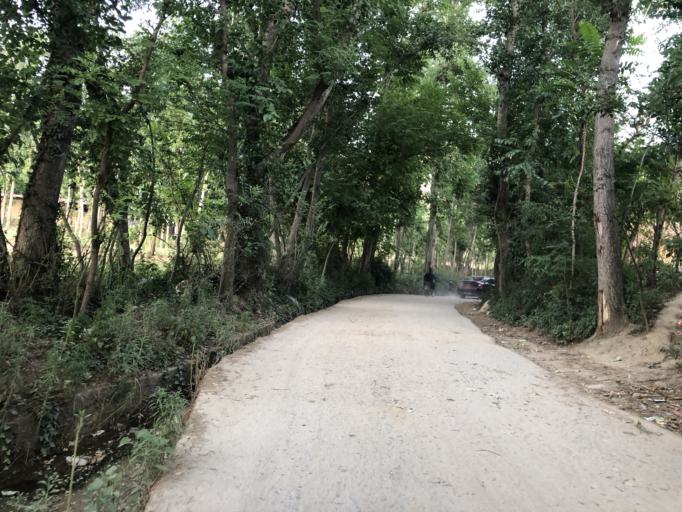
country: PK
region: Khyber Pakhtunkhwa
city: Daggar
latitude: 34.5802
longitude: 72.4542
